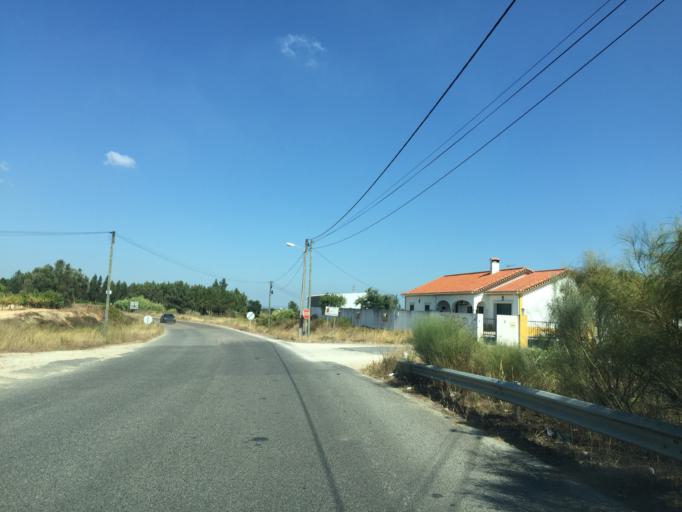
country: PT
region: Santarem
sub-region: Cartaxo
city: Pontevel
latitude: 39.1546
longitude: -8.8684
